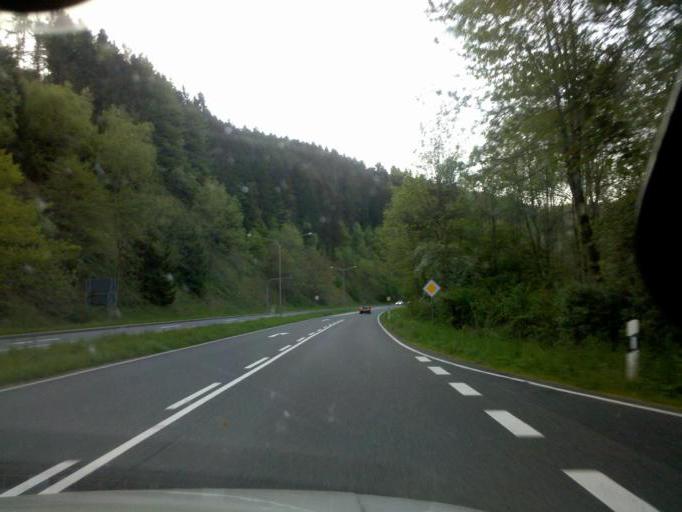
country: DE
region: North Rhine-Westphalia
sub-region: Regierungsbezirk Koln
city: Gummersbach
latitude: 50.9944
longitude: 7.5509
